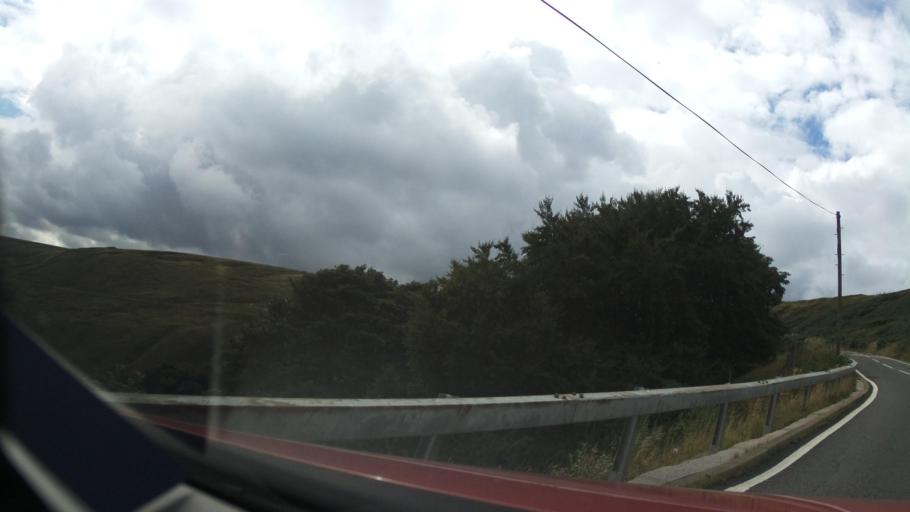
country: GB
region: England
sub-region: Kirklees
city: Meltham
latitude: 53.5361
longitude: -1.8529
